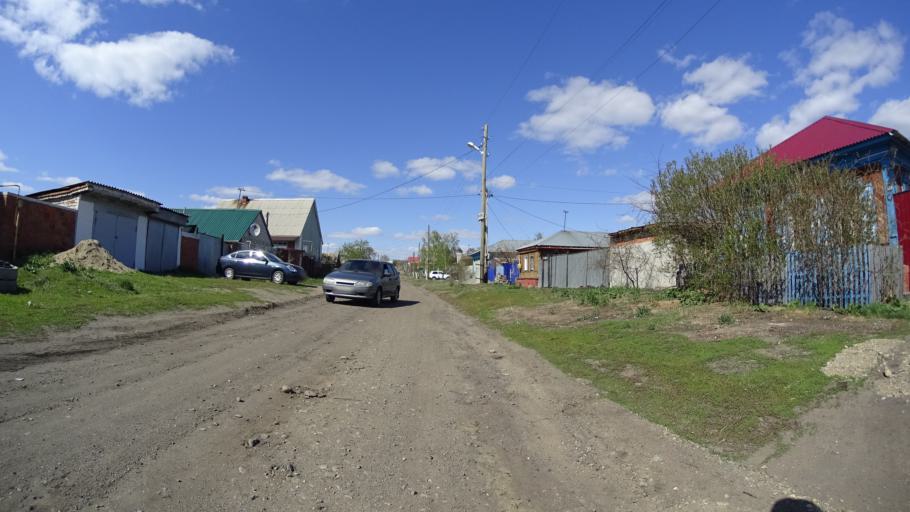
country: RU
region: Chelyabinsk
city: Troitsk
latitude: 54.0964
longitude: 61.5932
